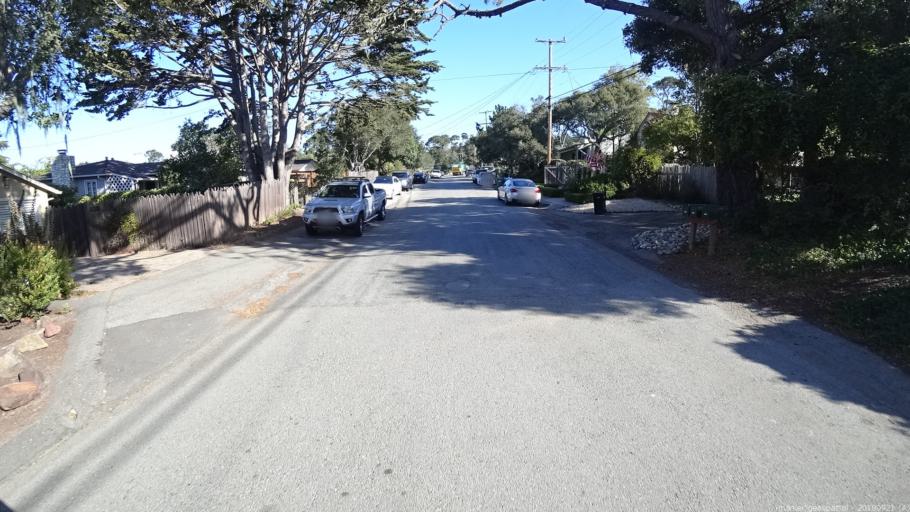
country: US
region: California
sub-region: Monterey County
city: Carmel-by-the-Sea
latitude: 36.5623
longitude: -121.9165
